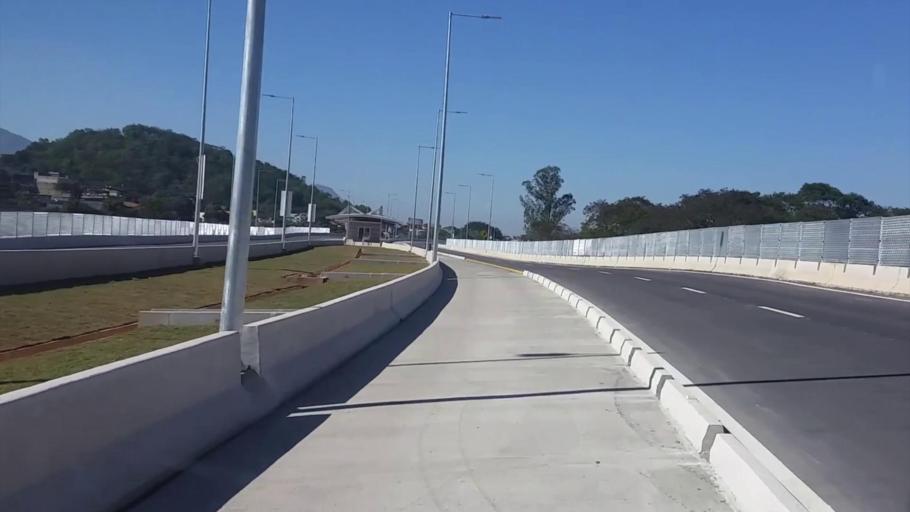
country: BR
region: Rio de Janeiro
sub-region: Nilopolis
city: Nilopolis
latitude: -22.9376
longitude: -43.3952
